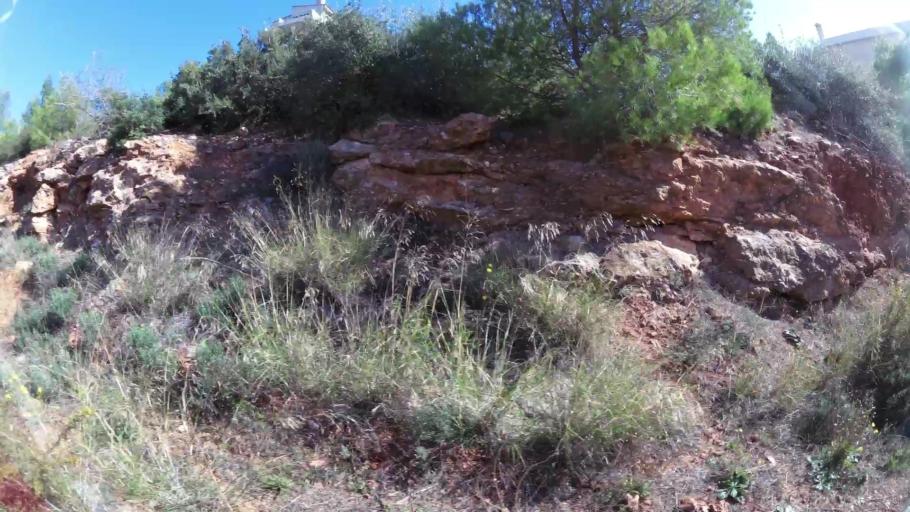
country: GR
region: Attica
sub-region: Nomarchia Anatolikis Attikis
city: Dioni
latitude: 38.0322
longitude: 23.9348
